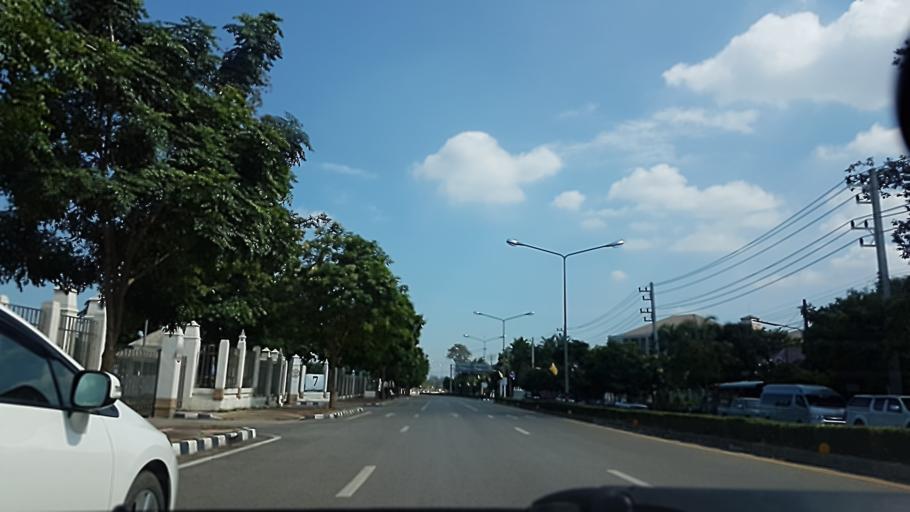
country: TH
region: Chiang Mai
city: Chiang Mai
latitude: 18.8250
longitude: 98.9599
